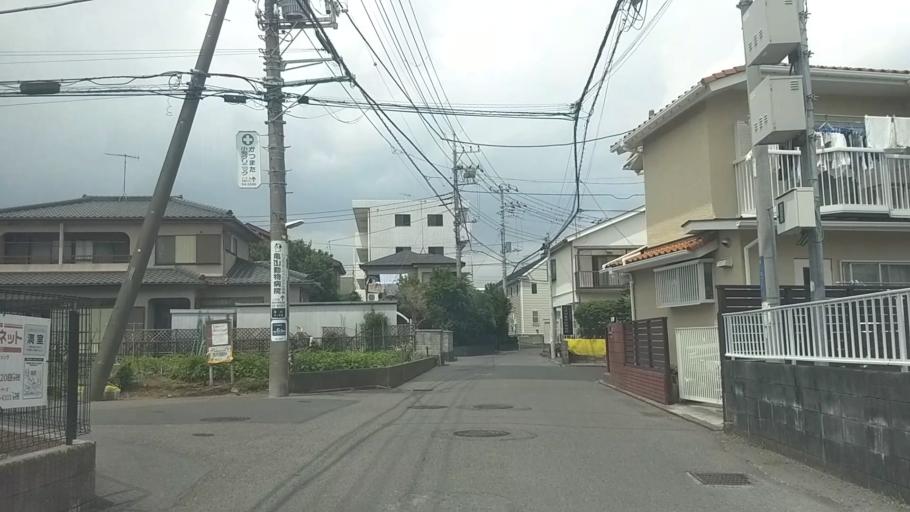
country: JP
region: Kanagawa
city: Chigasaki
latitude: 35.3557
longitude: 139.3982
